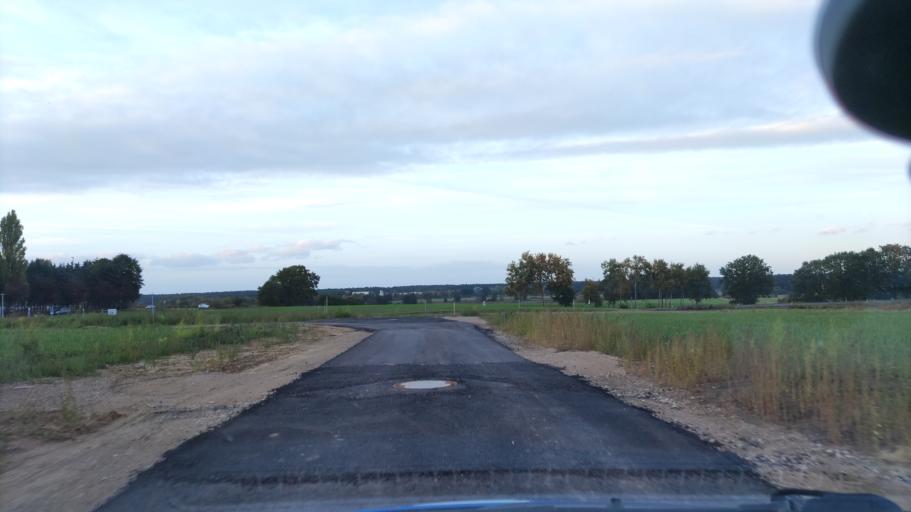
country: DE
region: Lower Saxony
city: Neetze
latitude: 53.2658
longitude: 10.6343
